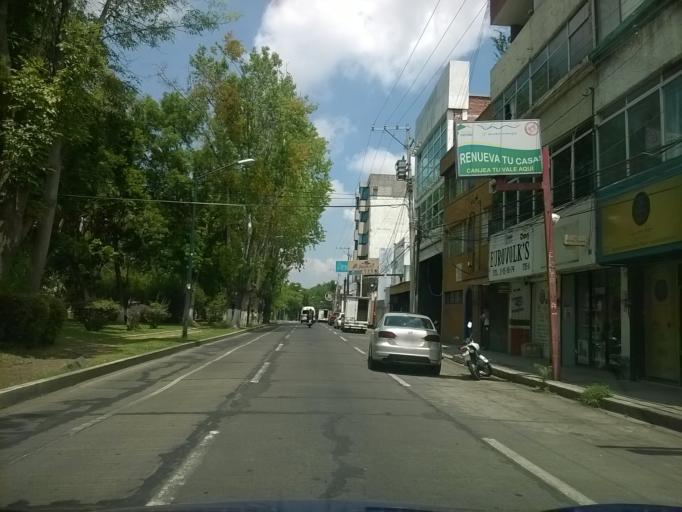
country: MX
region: Michoacan
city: Morelia
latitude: 19.6884
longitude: -101.1622
